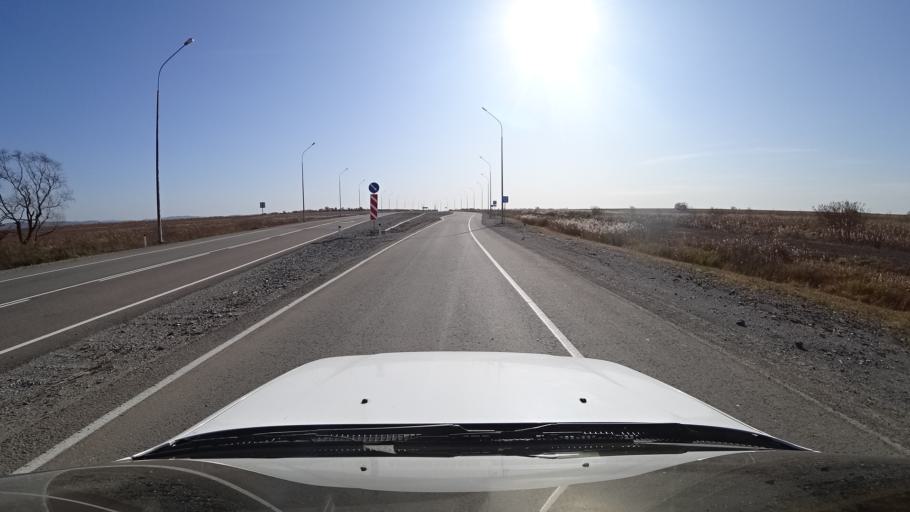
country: RU
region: Primorskiy
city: Dal'nerechensk
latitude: 45.8652
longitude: 133.7208
